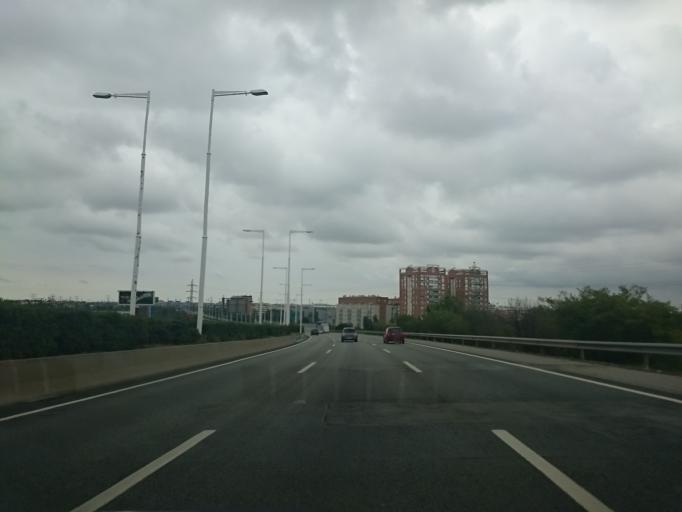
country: ES
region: Catalonia
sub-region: Provincia de Barcelona
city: Cornella de Llobregat
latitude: 41.3594
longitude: 2.0882
